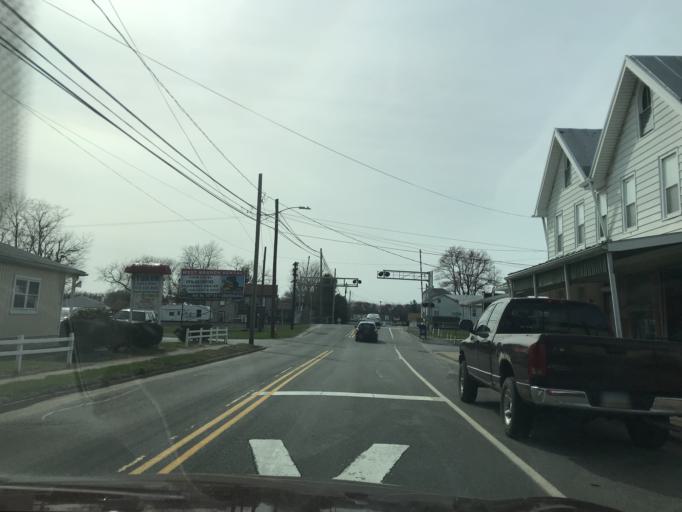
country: US
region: Pennsylvania
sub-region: Union County
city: Lewisburg
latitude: 40.9661
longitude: -76.8569
